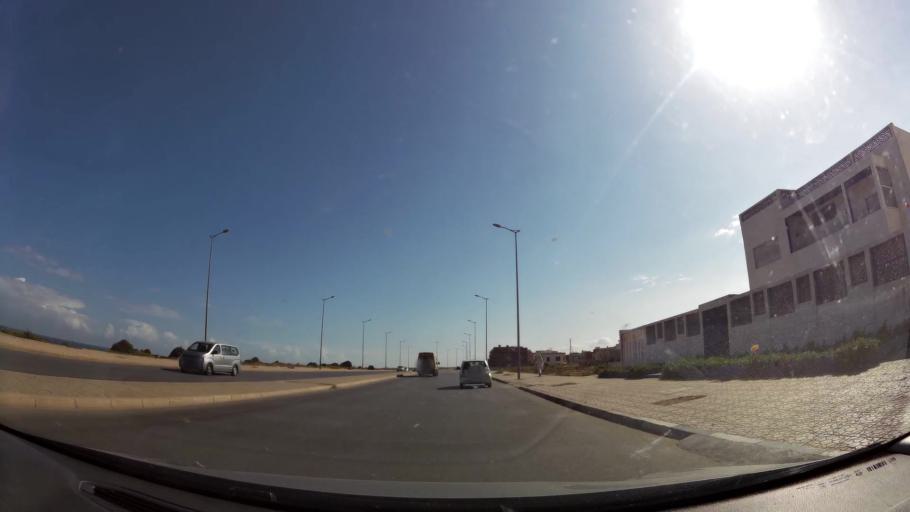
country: MA
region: Rabat-Sale-Zemmour-Zaer
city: Sale
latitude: 34.0715
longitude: -6.8024
